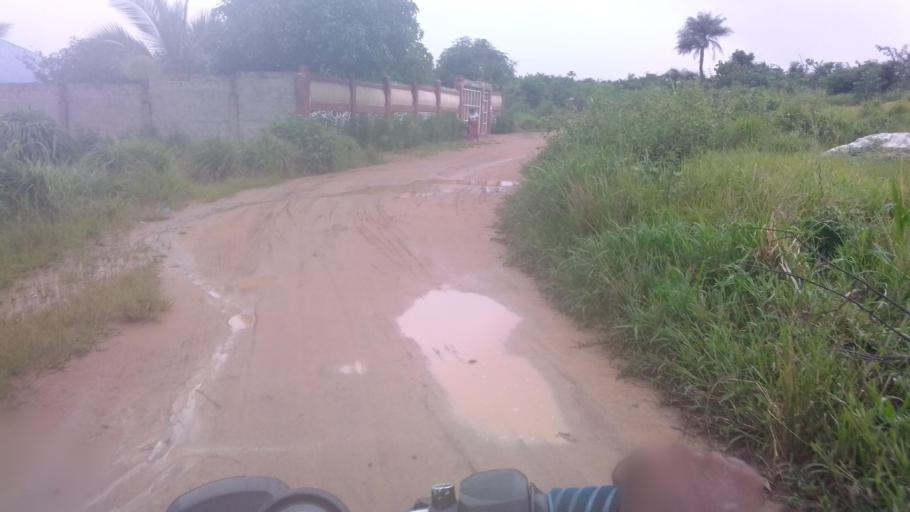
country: SL
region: Eastern Province
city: Kenema
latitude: 7.8322
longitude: -11.2121
